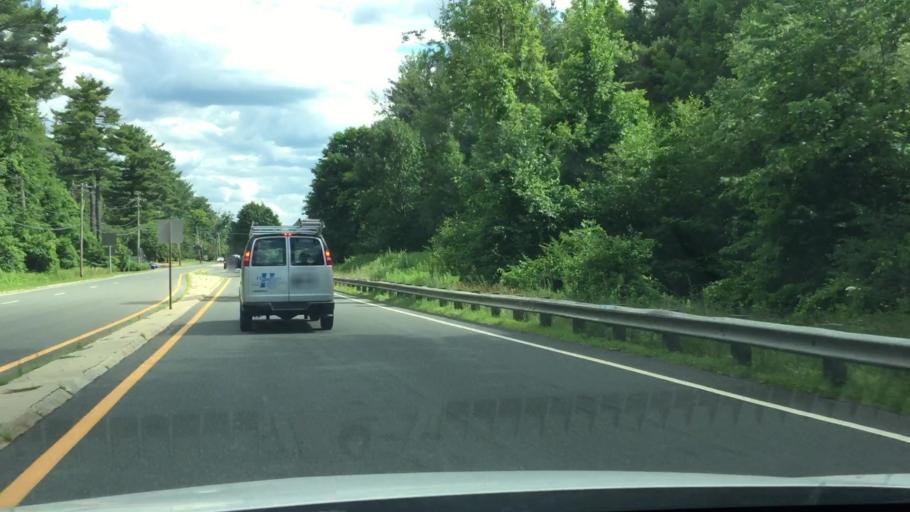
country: US
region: Massachusetts
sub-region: Berkshire County
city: Lenox
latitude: 42.3426
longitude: -73.2698
